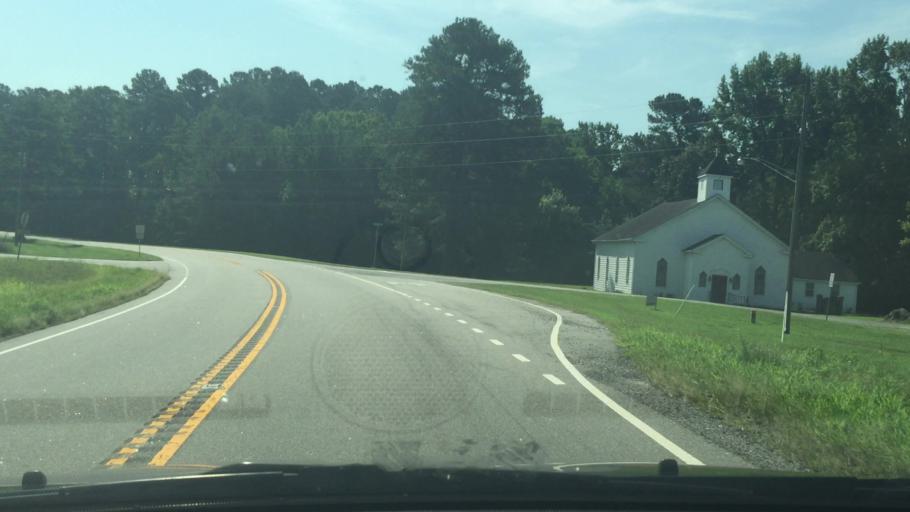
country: US
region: Virginia
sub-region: Southampton County
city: Courtland
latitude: 36.7849
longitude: -77.1270
